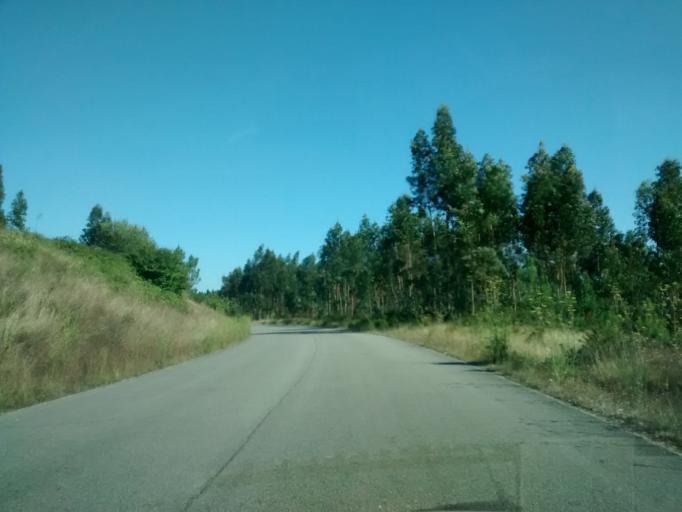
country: PT
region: Coimbra
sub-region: Cantanhede
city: Cantanhede
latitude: 40.4249
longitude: -8.6212
